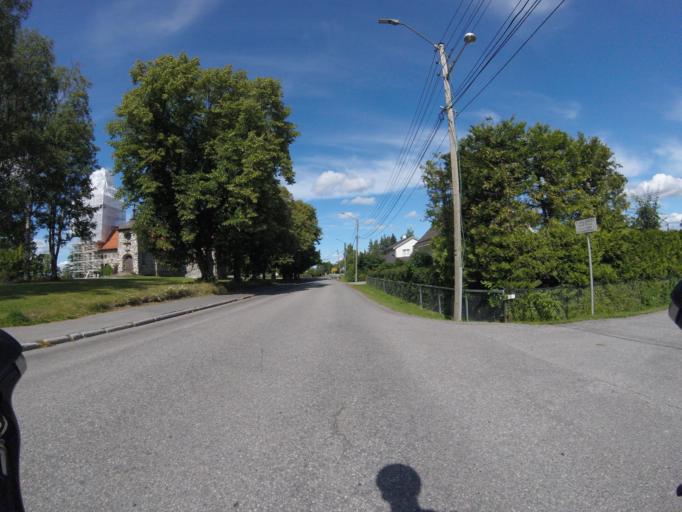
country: NO
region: Akershus
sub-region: Skedsmo
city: Lillestrom
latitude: 59.9522
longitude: 11.0157
